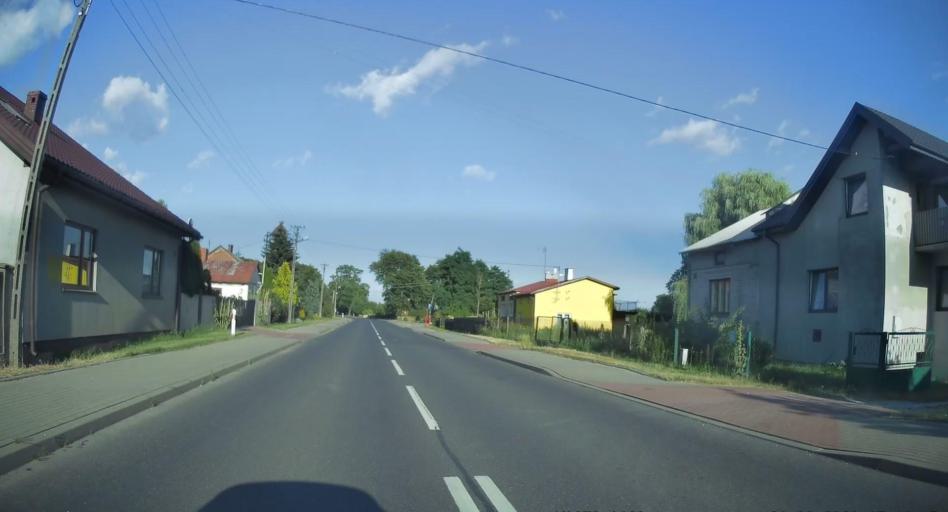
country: PL
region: Lodz Voivodeship
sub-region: Powiat rawski
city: Biala Rawska
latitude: 51.7993
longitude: 20.5230
